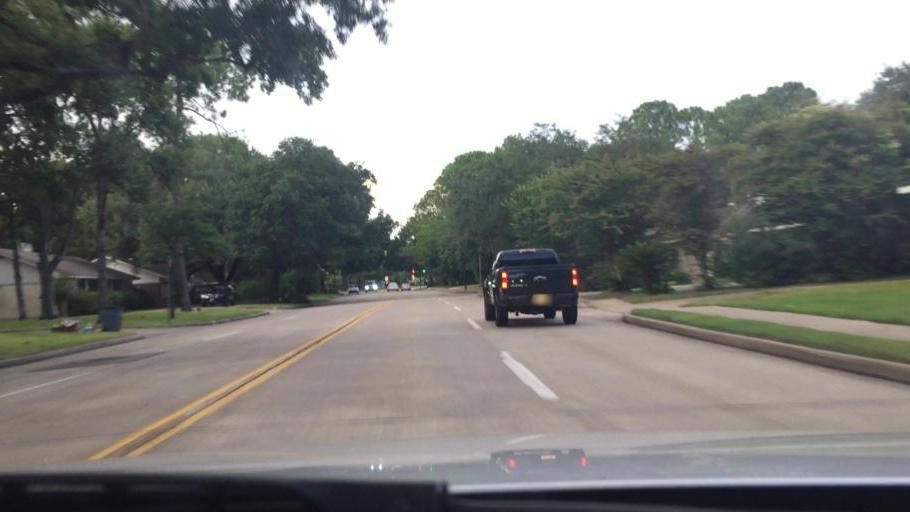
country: US
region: Texas
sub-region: Harris County
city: Hunters Creek Village
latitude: 29.7472
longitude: -95.4773
